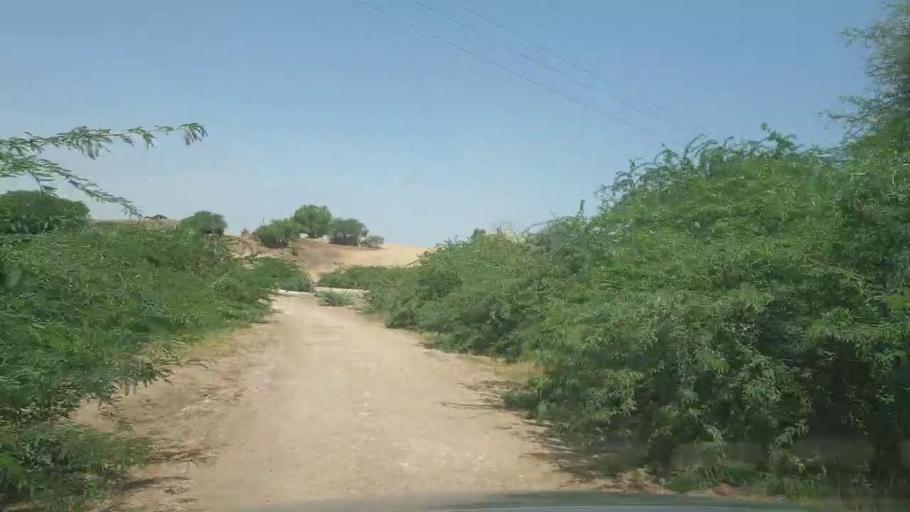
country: PK
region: Sindh
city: Kot Diji
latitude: 27.3256
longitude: 69.0123
